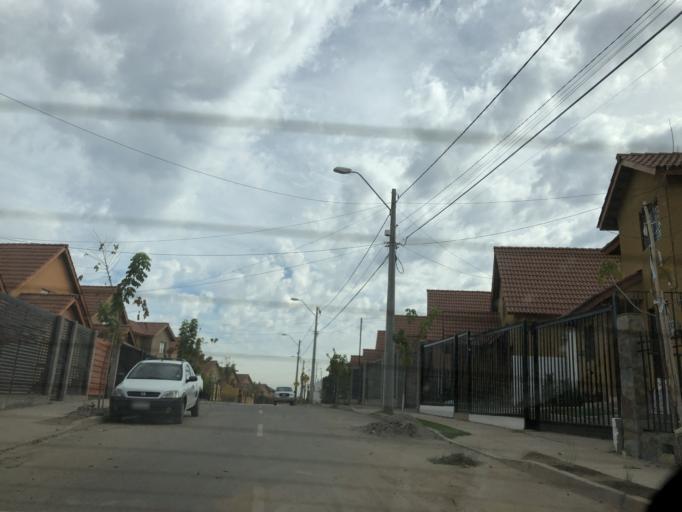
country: CL
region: Santiago Metropolitan
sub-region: Provincia de Cordillera
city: Puente Alto
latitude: -33.5863
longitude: -70.5299
